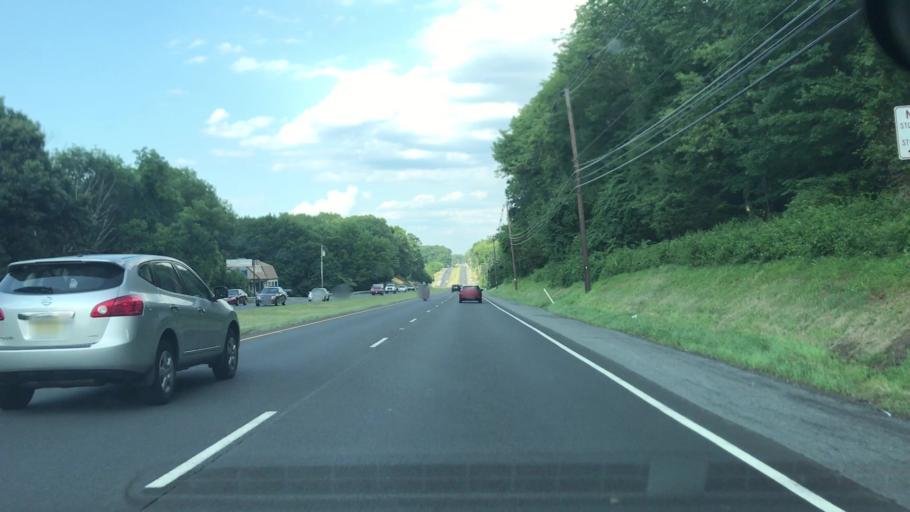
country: US
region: New Jersey
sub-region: Hunterdon County
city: Whitehouse Station
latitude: 40.5378
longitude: -74.7655
